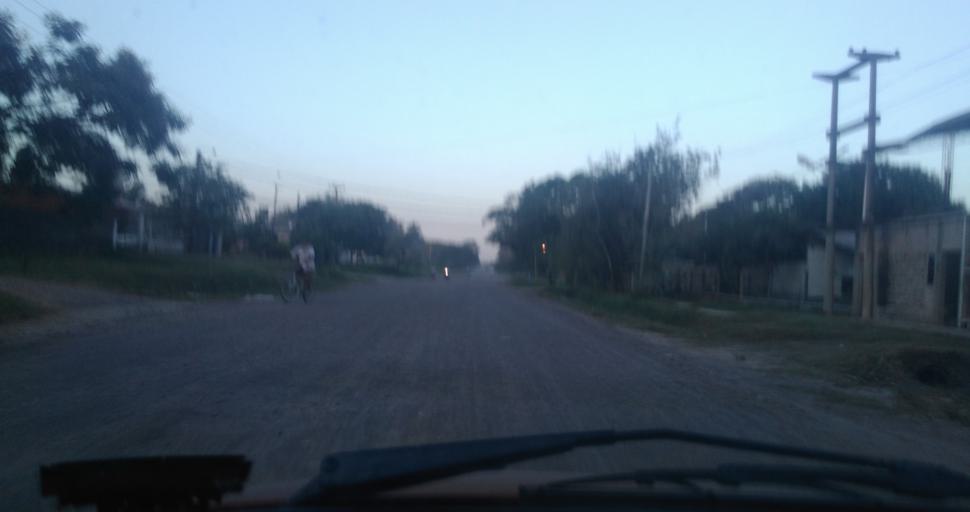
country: AR
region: Chaco
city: Resistencia
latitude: -27.4914
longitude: -58.9742
